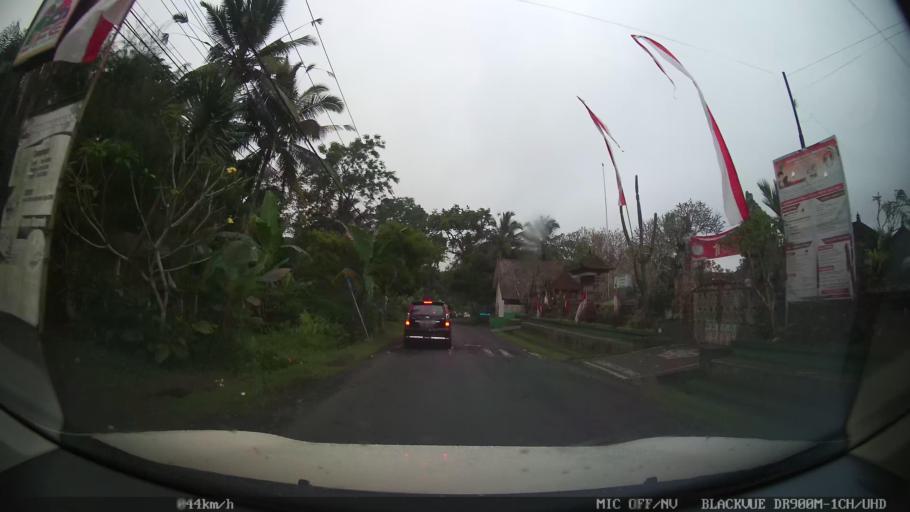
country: ID
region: Bali
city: Banjar Ponggang
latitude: -8.3810
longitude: 115.2654
